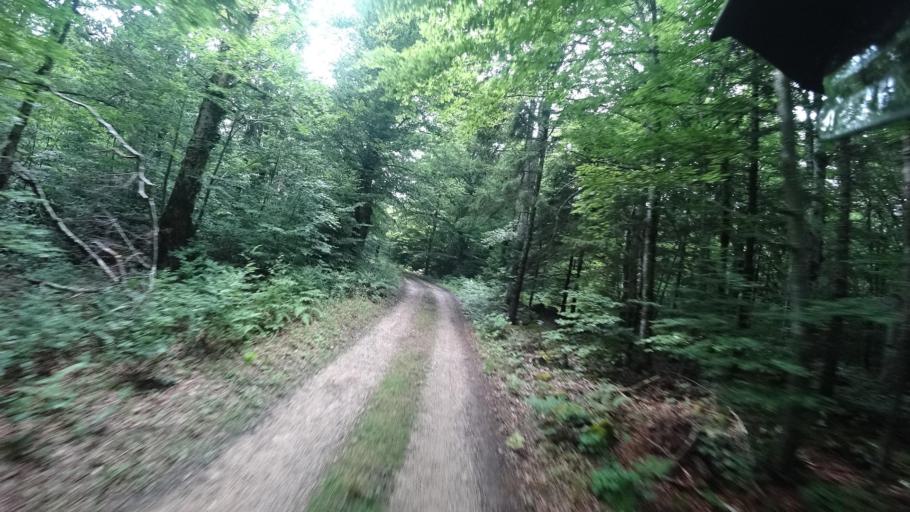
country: HR
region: Licko-Senjska
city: Jezerce
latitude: 44.7828
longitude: 15.6451
